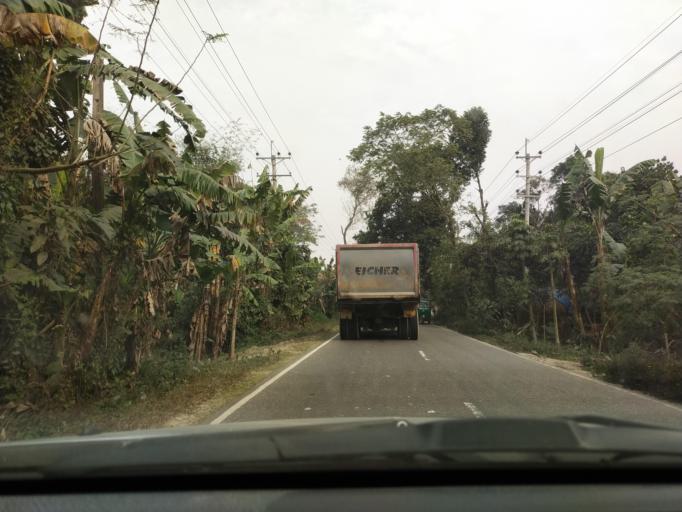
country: BD
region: Dhaka
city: Narsingdi
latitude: 24.0222
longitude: 90.7380
